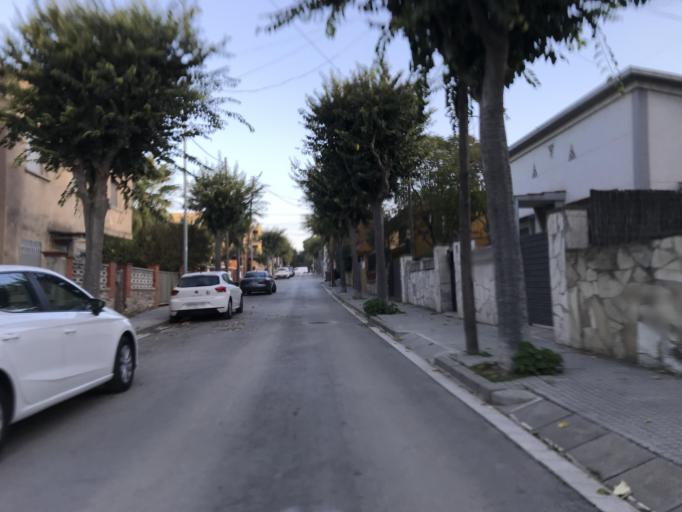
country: ES
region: Catalonia
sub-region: Provincia de Barcelona
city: Parets del Valles
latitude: 41.5603
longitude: 2.2218
